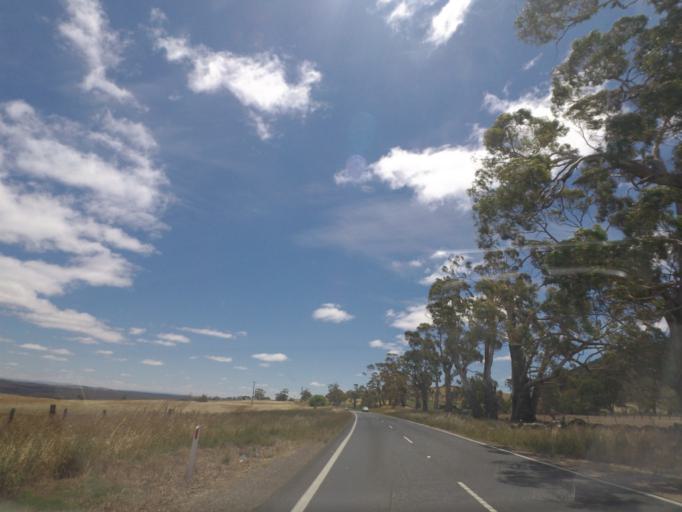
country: AU
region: Victoria
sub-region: Mount Alexander
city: Castlemaine
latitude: -37.2740
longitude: 144.1468
